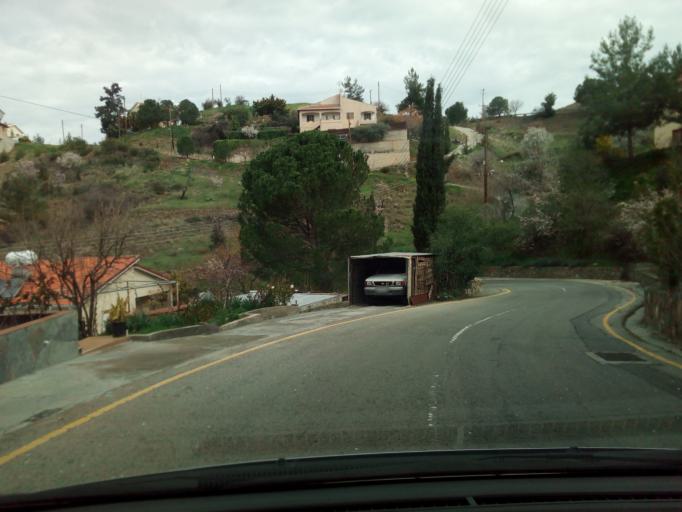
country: CY
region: Lefkosia
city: Klirou
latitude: 34.9580
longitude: 33.1590
